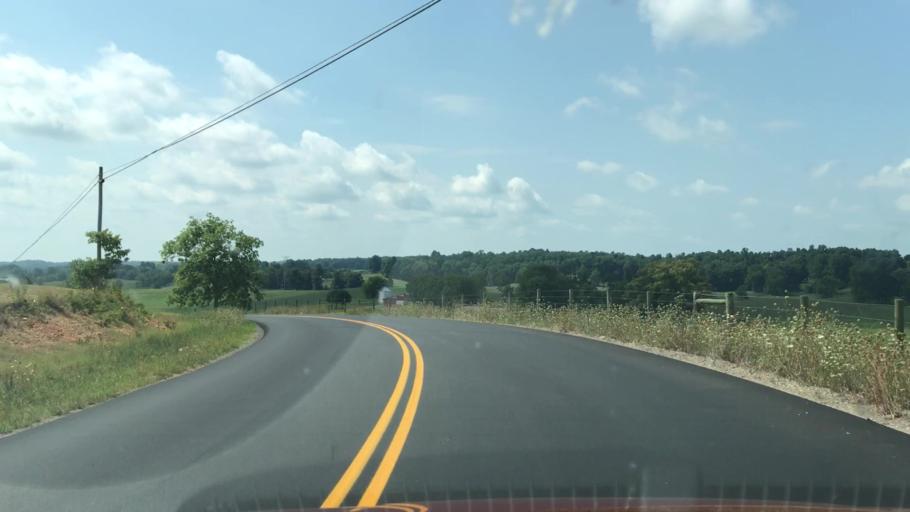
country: US
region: Kentucky
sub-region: Monroe County
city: Tompkinsville
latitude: 36.8000
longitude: -85.8201
